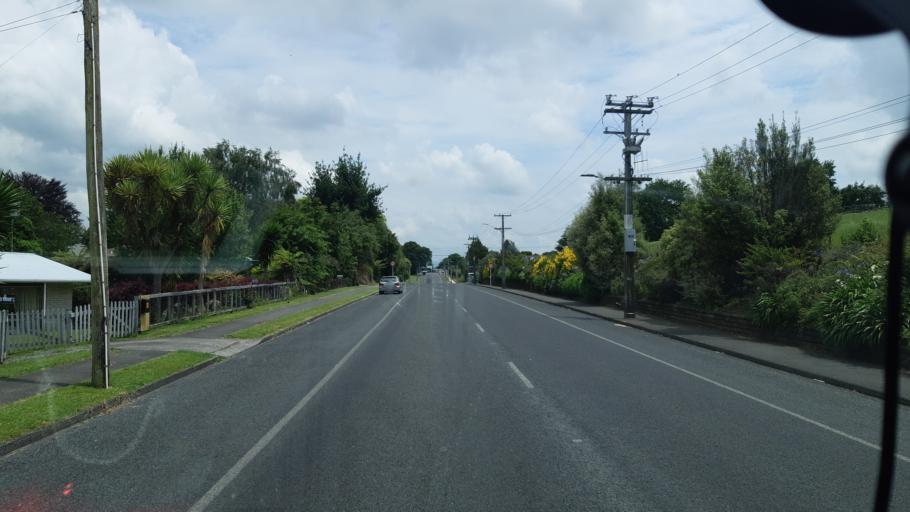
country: NZ
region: Waikato
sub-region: Waipa District
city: Cambridge
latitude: -38.0398
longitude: 175.3511
